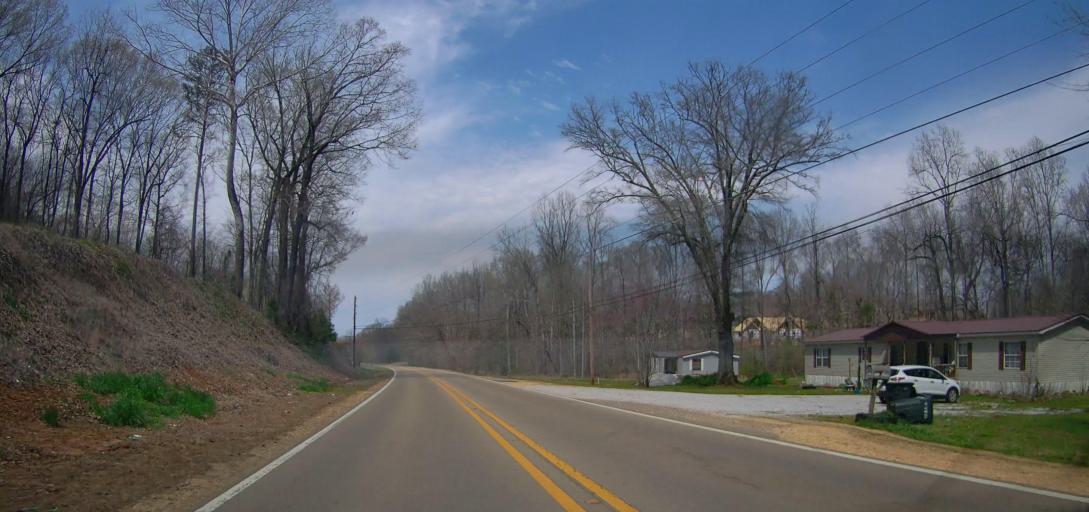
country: US
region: Mississippi
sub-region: Union County
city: New Albany
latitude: 34.4645
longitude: -88.9820
